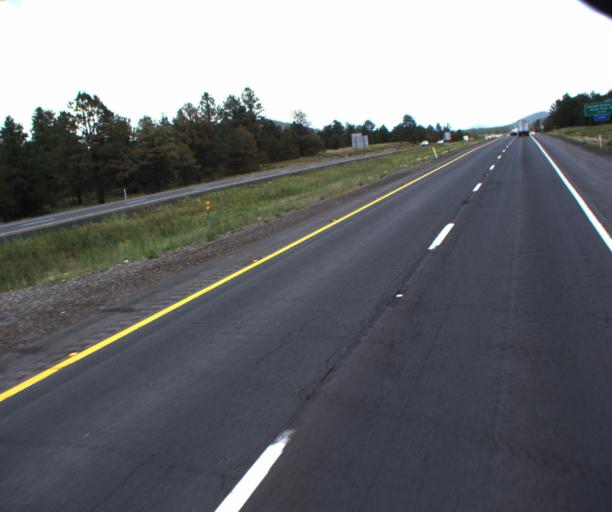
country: US
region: Arizona
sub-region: Coconino County
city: Williams
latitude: 35.2579
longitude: -112.1372
